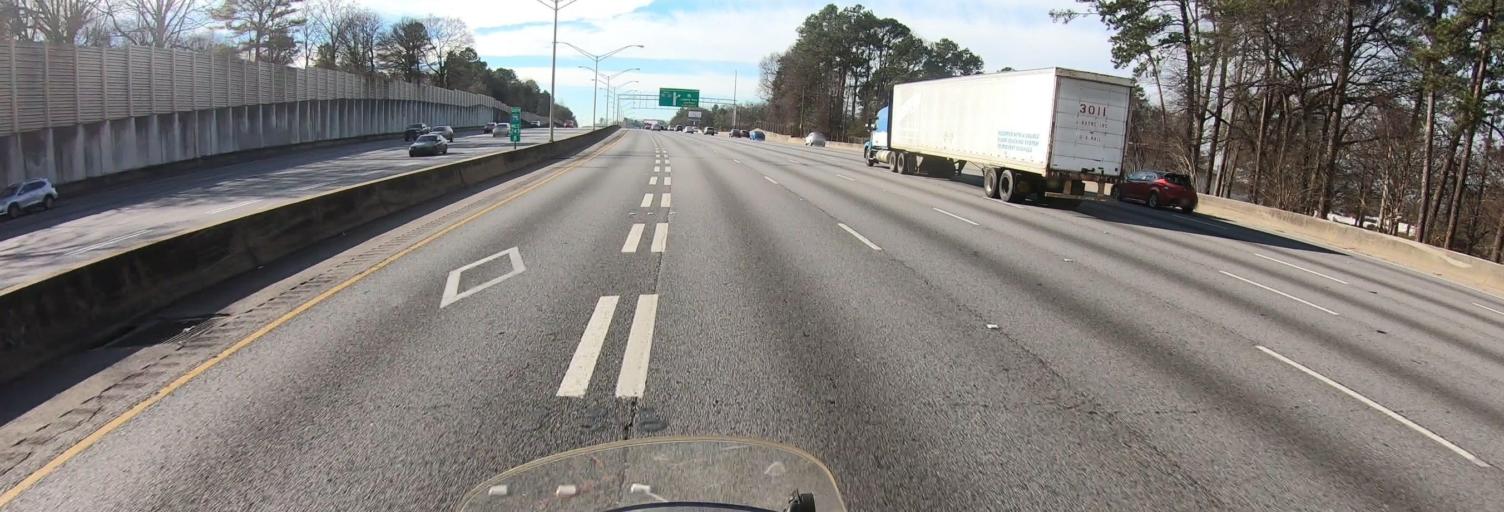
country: US
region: Georgia
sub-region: Fulton County
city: Atlanta
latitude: 33.7096
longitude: -84.3995
